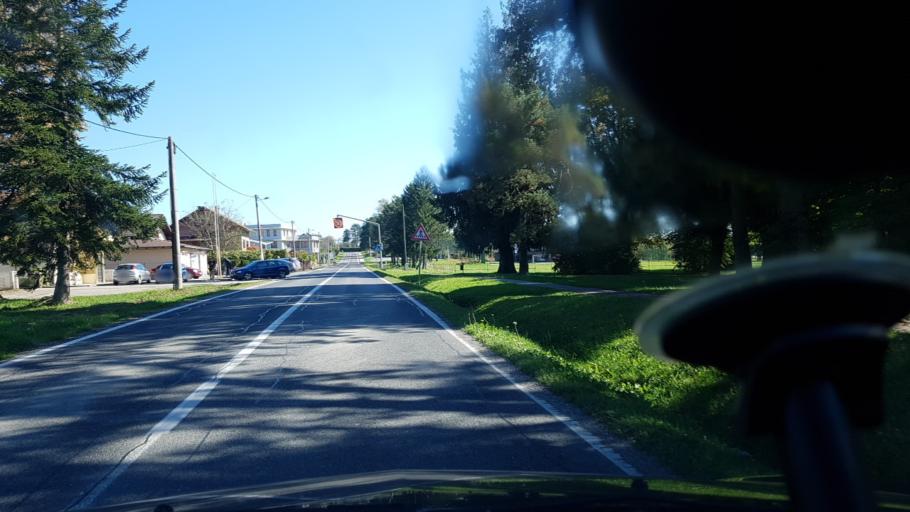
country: HR
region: Zagrebacka
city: Kriz
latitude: 45.7096
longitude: 16.4742
